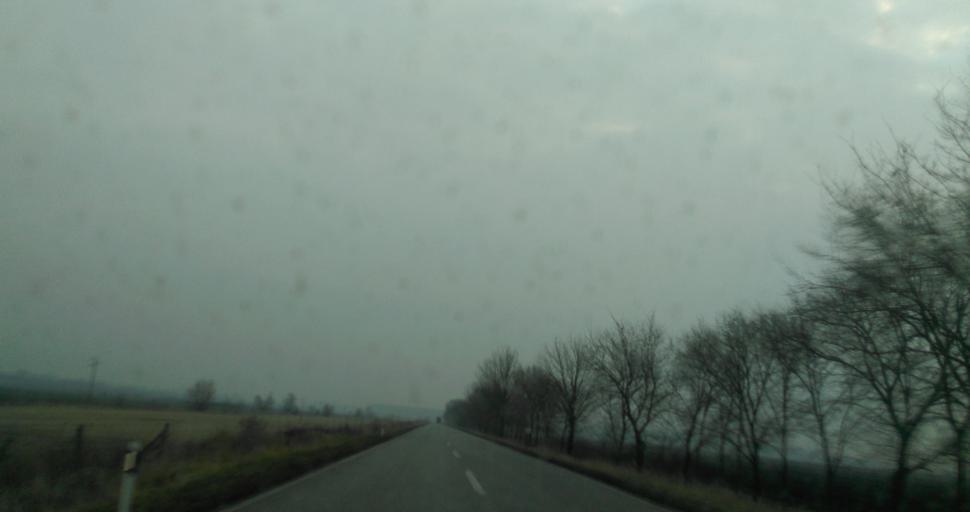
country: RS
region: Autonomna Pokrajina Vojvodina
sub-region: Srednjebanatski Okrug
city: Novi Becej
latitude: 45.5831
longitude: 20.0933
